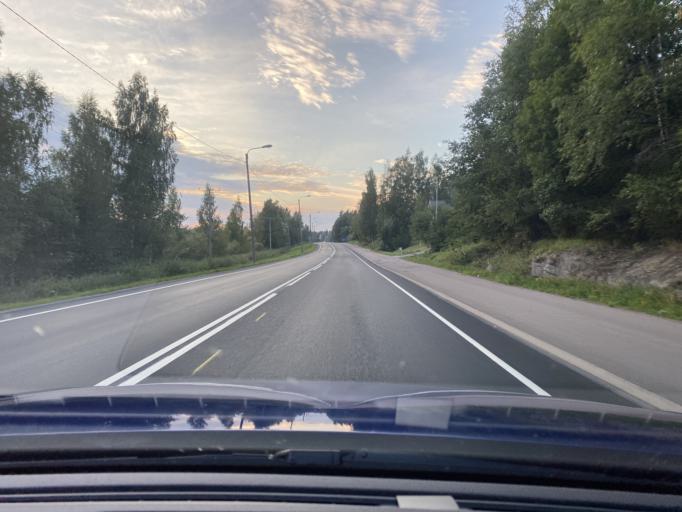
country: FI
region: Satakunta
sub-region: Pohjois-Satakunta
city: Kankaanpaeae
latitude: 61.8208
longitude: 22.3656
